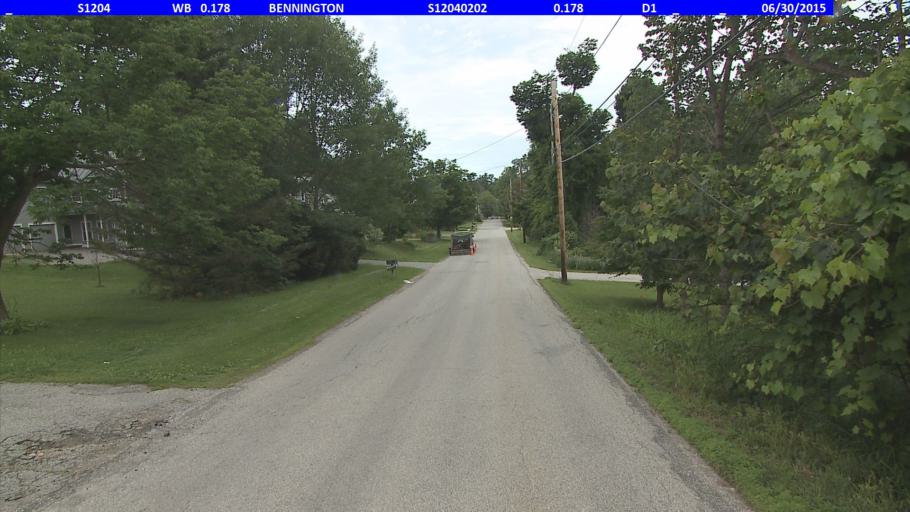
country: US
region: Vermont
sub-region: Bennington County
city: North Bennington
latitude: 42.9281
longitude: -73.2374
